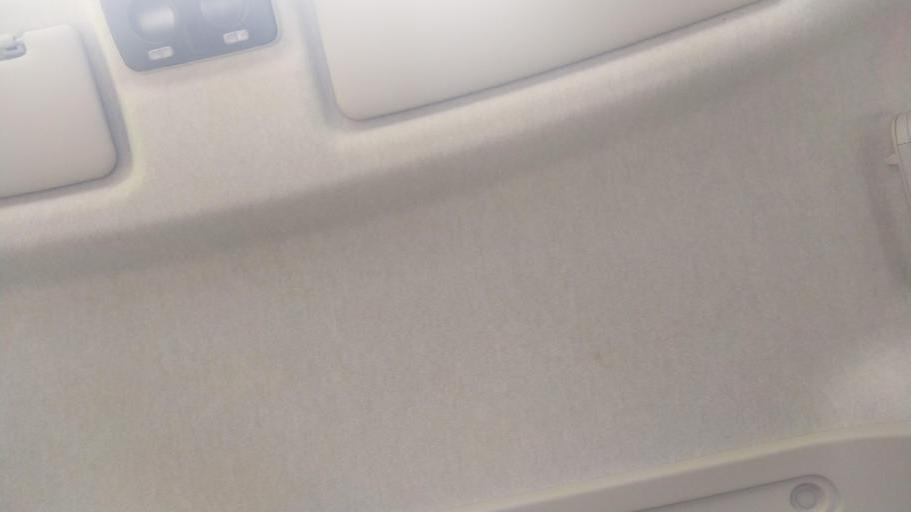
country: GB
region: England
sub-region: Somerset
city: Yeovil
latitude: 50.8380
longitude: -2.6011
